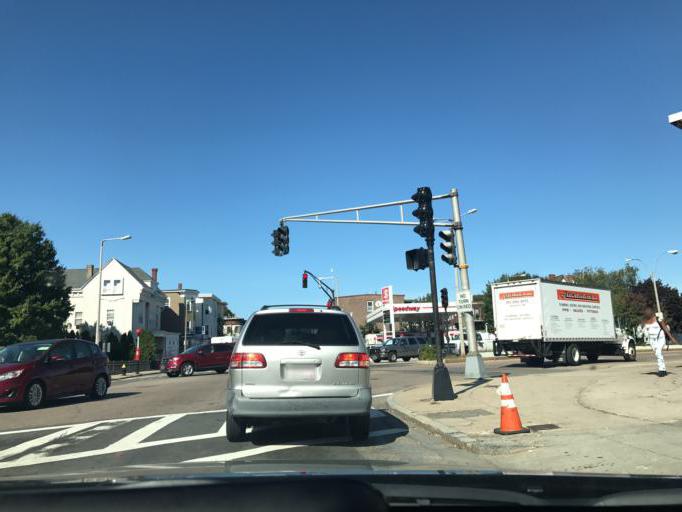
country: US
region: Massachusetts
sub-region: Suffolk County
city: South Boston
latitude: 42.3205
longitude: -71.0566
